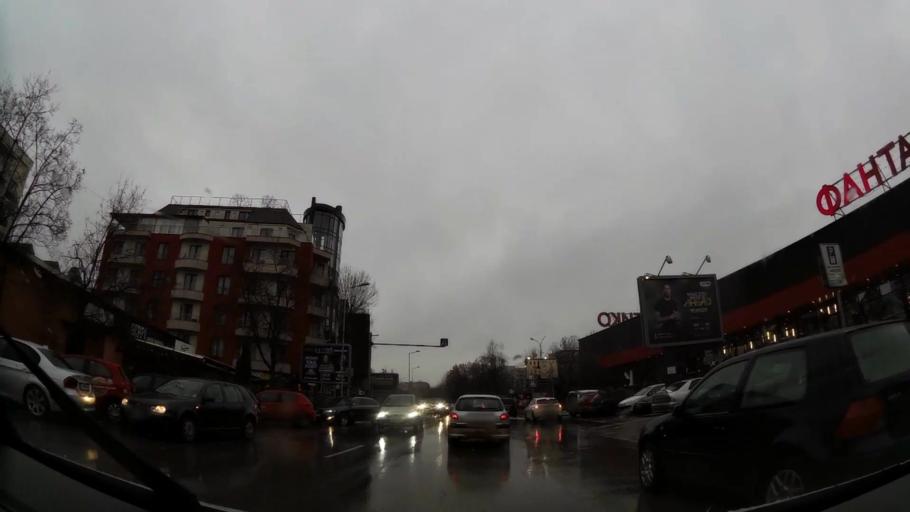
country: BG
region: Sofia-Capital
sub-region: Stolichna Obshtina
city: Sofia
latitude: 42.6503
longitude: 23.3420
